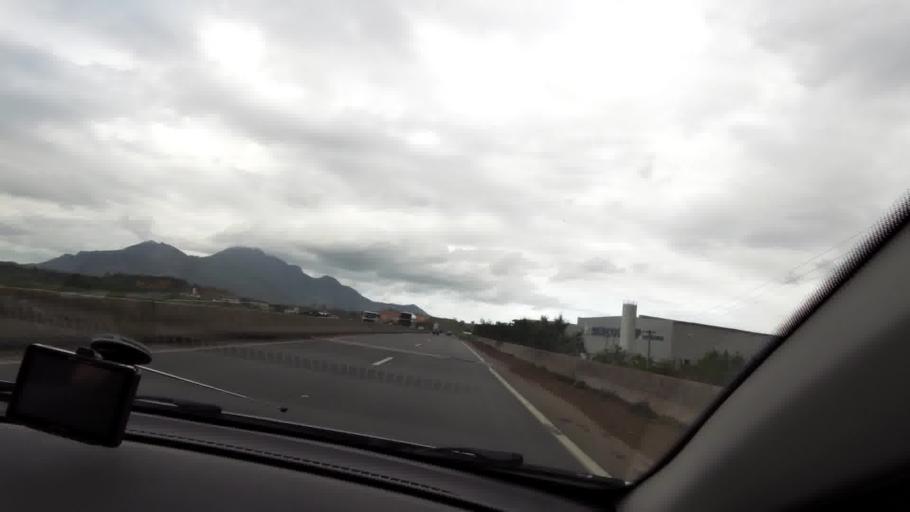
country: BR
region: Espirito Santo
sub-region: Vitoria
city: Vitoria
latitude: -20.2253
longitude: -40.3619
